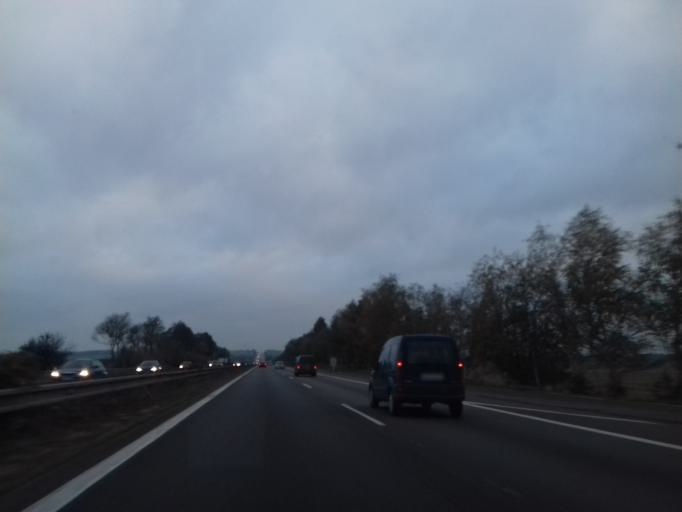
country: CZ
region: Central Bohemia
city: Zruc nad Sazavou
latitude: 49.6738
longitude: 15.1168
